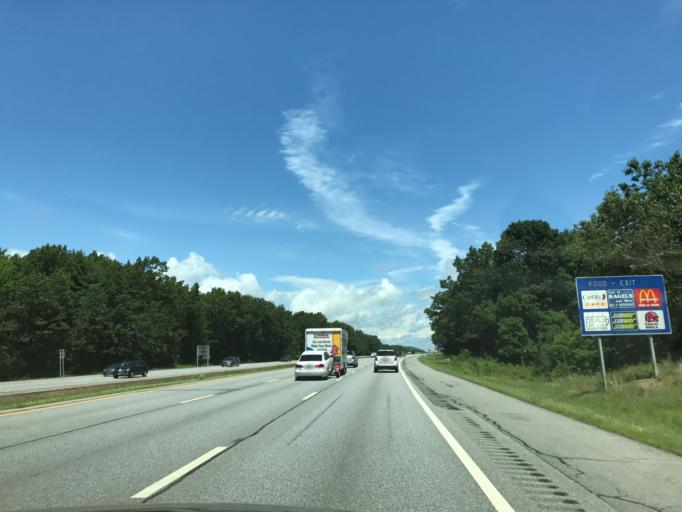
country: US
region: New York
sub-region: Warren County
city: West Glens Falls
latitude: 43.2901
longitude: -73.6808
